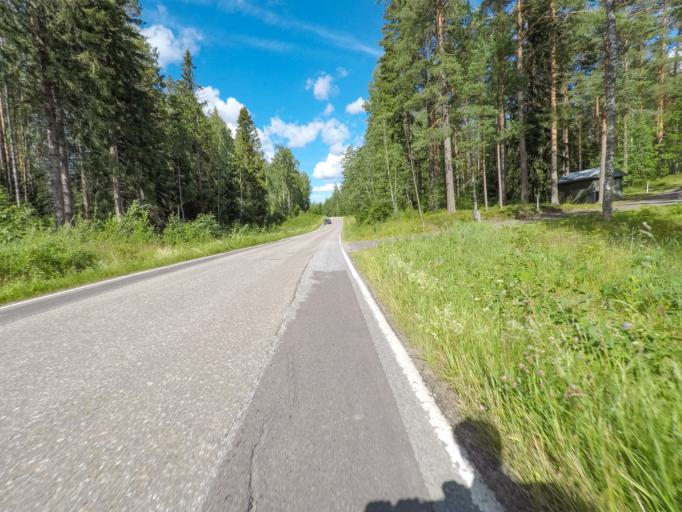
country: FI
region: South Karelia
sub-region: Lappeenranta
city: Joutseno
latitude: 61.0972
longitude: 28.3599
